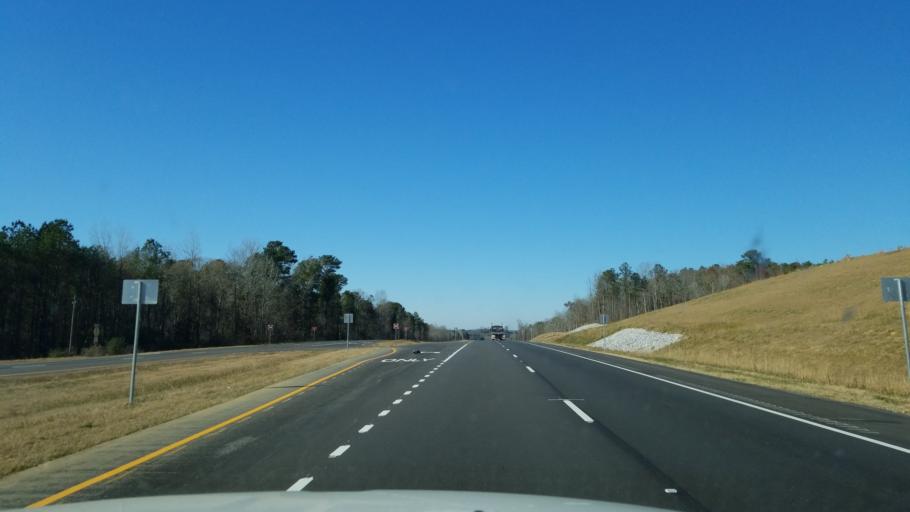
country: US
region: Alabama
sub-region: Pickens County
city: Reform
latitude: 33.3599
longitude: -87.9723
